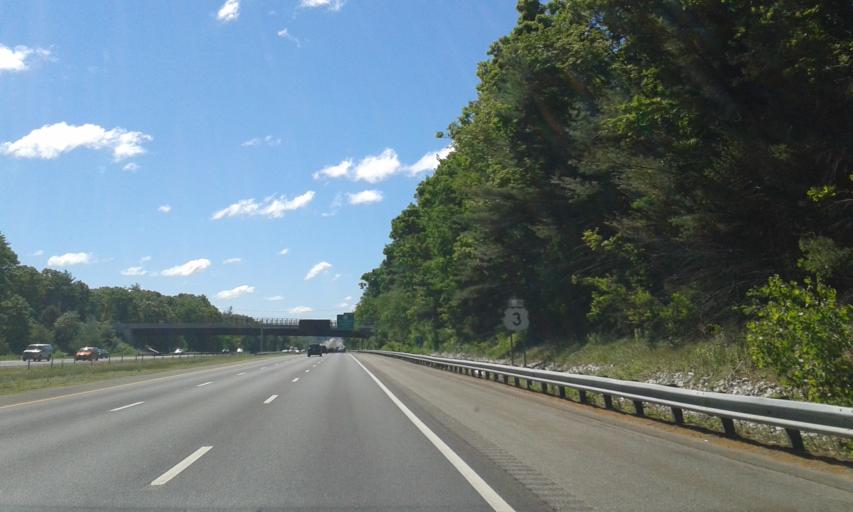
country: US
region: Massachusetts
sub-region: Middlesex County
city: Bedford
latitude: 42.5199
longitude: -71.2615
